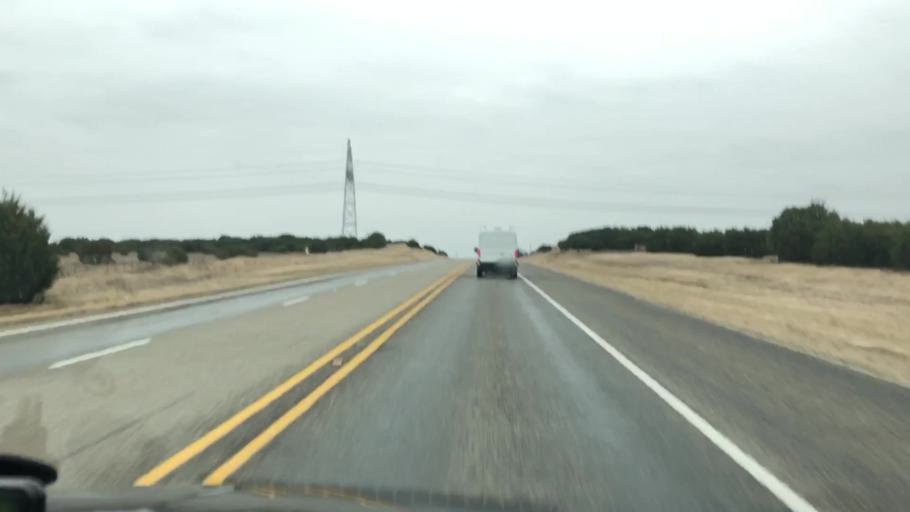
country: US
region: Texas
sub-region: Lampasas County
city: Lampasas
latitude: 31.1416
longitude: -98.1843
